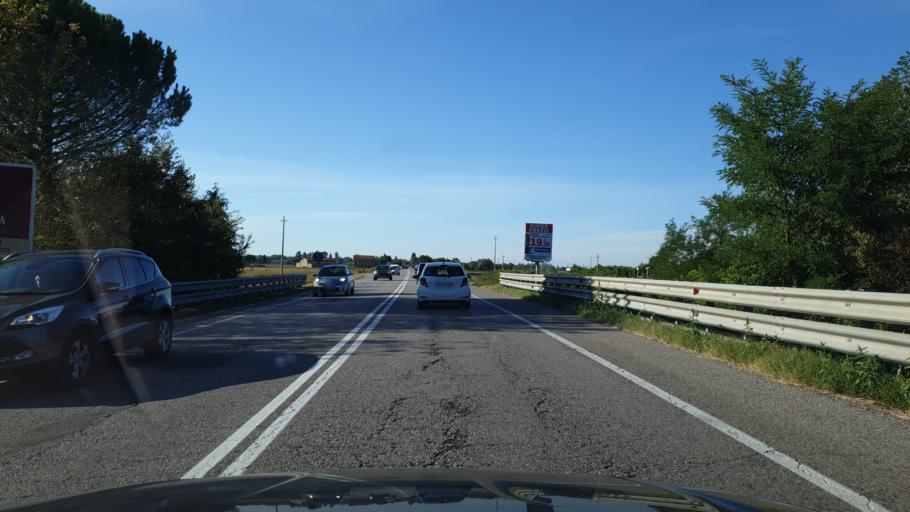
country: IT
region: Emilia-Romagna
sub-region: Provincia di Ravenna
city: Fosso Ghiaia
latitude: 44.3614
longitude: 12.2543
